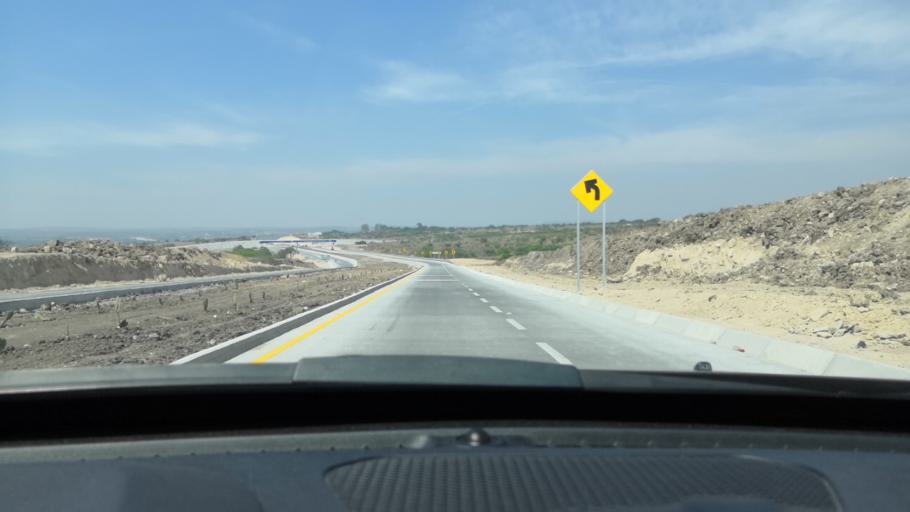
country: MX
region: Guanajuato
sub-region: San Francisco del Rincon
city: Estacion de San Francisco
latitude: 21.0871
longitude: -101.8172
